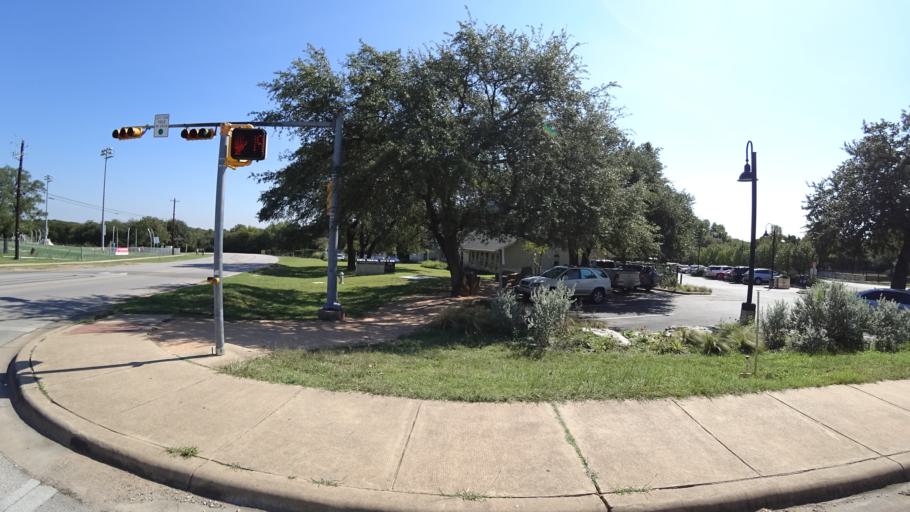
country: US
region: Texas
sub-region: Travis County
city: Rollingwood
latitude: 30.2742
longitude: -97.8122
